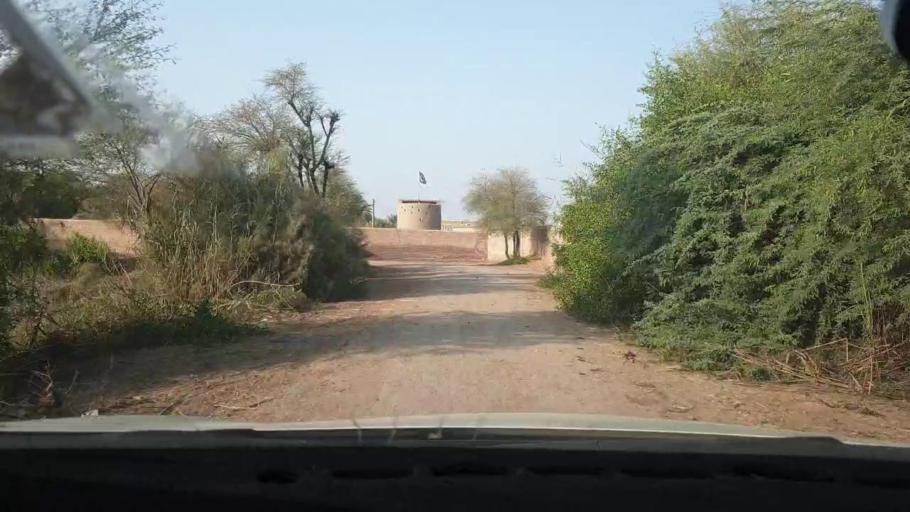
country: PK
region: Sindh
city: Berani
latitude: 25.8183
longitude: 68.7945
